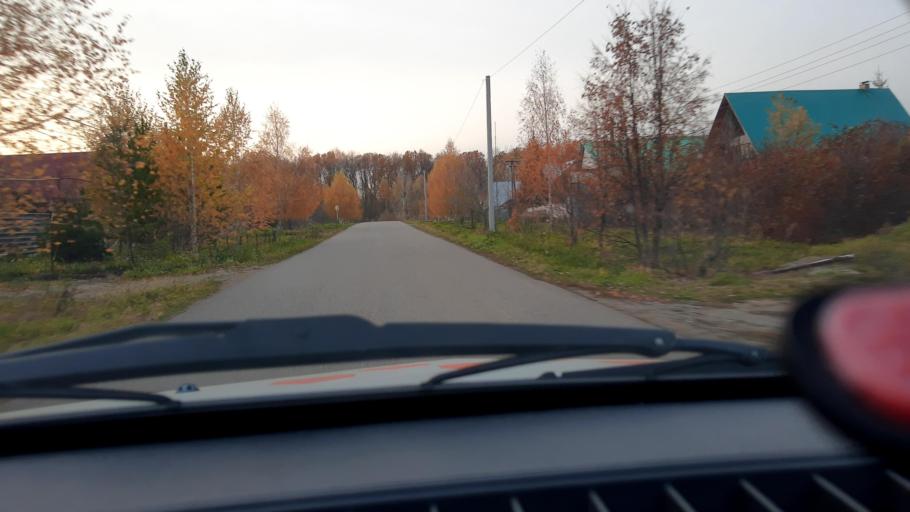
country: RU
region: Bashkortostan
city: Iglino
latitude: 54.7957
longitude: 56.3149
